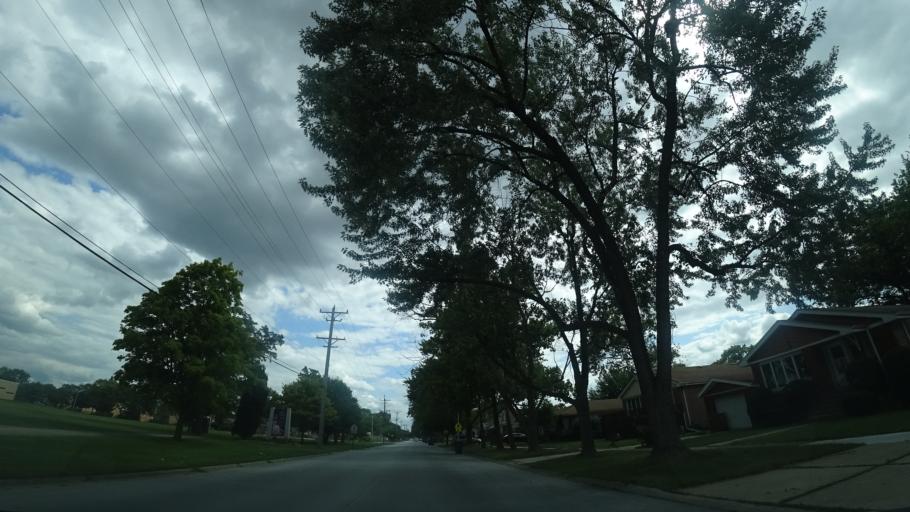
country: US
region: Illinois
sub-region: Cook County
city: Alsip
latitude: 41.6971
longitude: -87.7303
